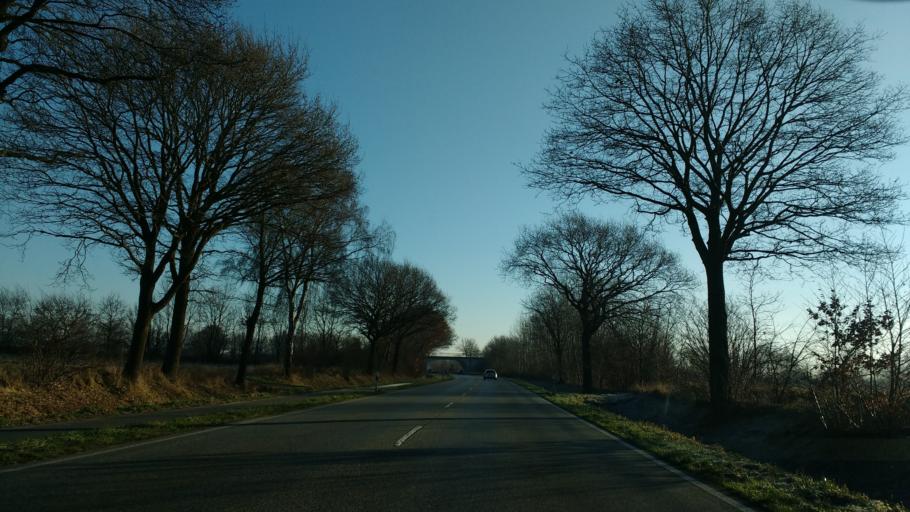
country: DE
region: Schleswig-Holstein
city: Wasbek
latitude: 54.0699
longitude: 9.8791
